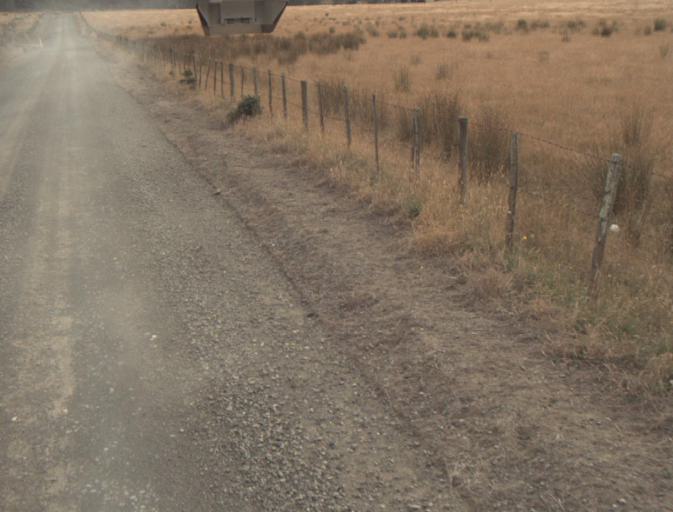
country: AU
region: Tasmania
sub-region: Northern Midlands
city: Evandale
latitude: -41.4720
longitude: 147.4464
